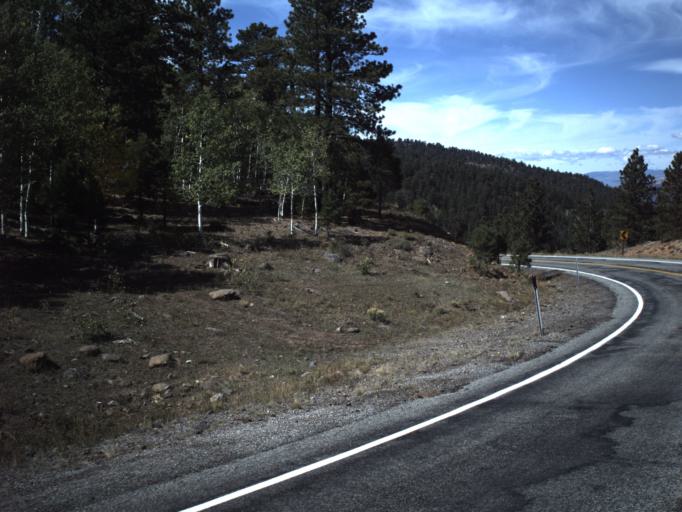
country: US
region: Utah
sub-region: Wayne County
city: Loa
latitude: 38.1469
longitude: -111.3268
